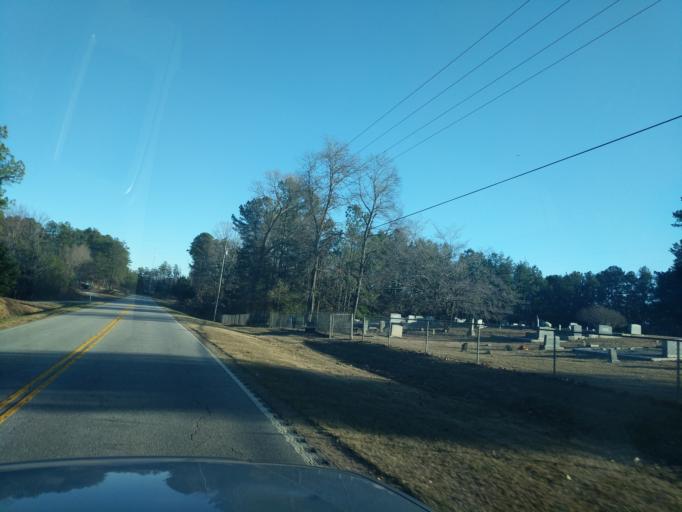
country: US
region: South Carolina
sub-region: Oconee County
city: Westminster
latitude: 34.7029
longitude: -83.1919
